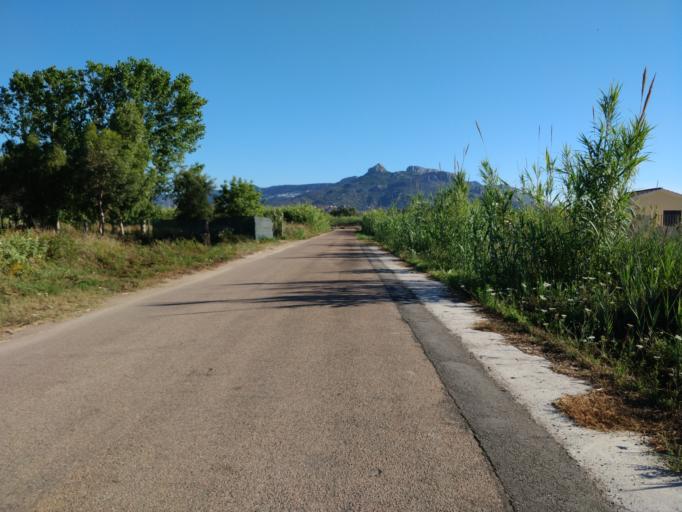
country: IT
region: Sardinia
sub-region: Provincia di Ogliastra
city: Lotzorai
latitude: 39.9592
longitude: 9.6774
